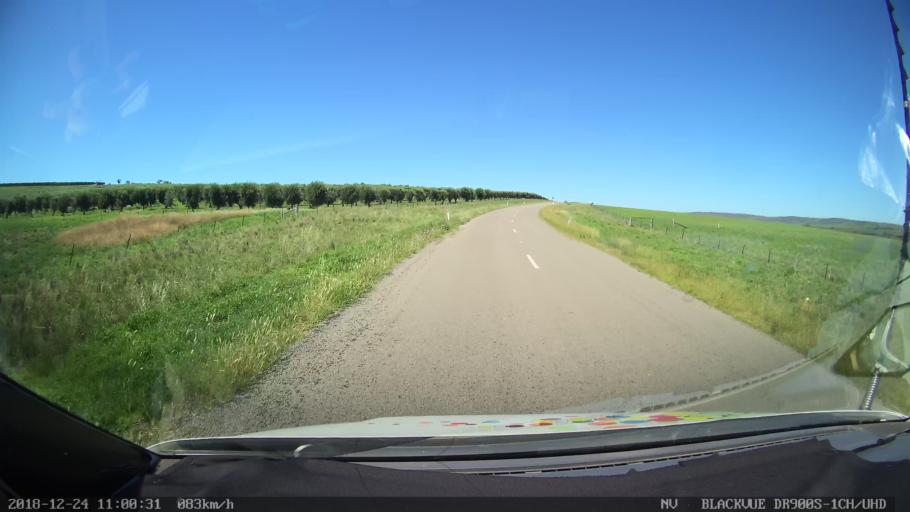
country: AU
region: New South Wales
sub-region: Upper Hunter Shire
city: Merriwa
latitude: -32.0686
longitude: 150.3936
